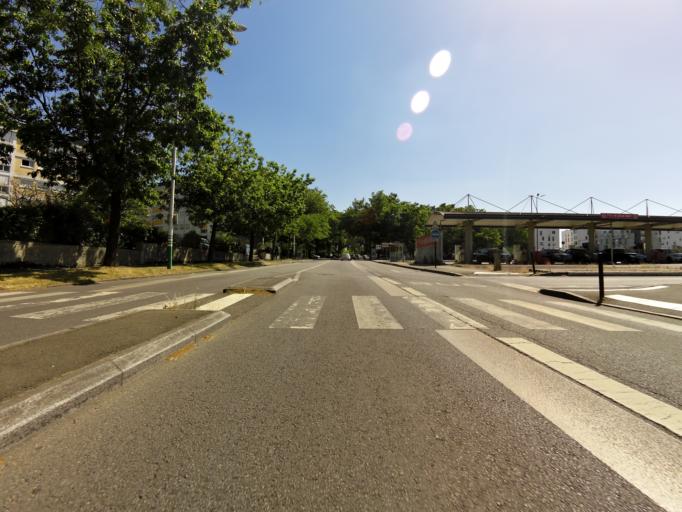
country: FR
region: Pays de la Loire
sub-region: Departement de la Loire-Atlantique
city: Saint-Herblain
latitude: 47.2226
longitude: -1.6028
